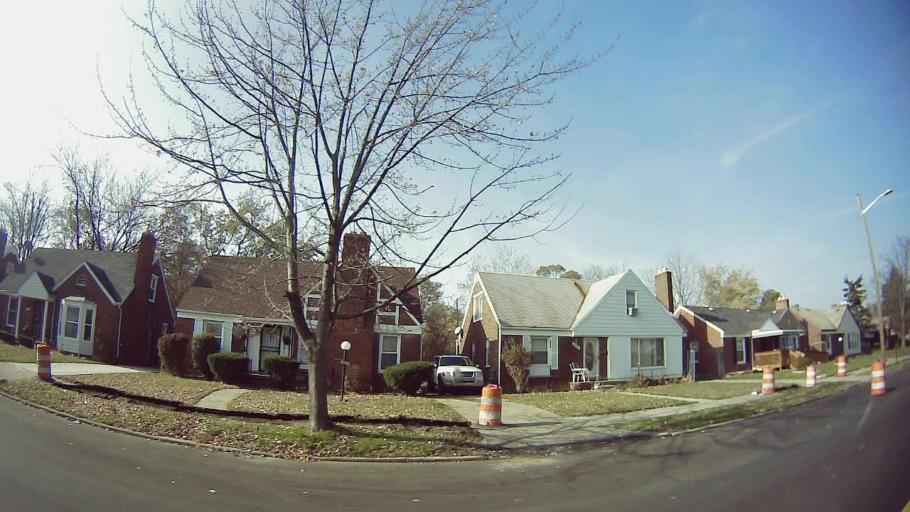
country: US
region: Michigan
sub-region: Oakland County
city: Oak Park
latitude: 42.4295
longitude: -83.1899
